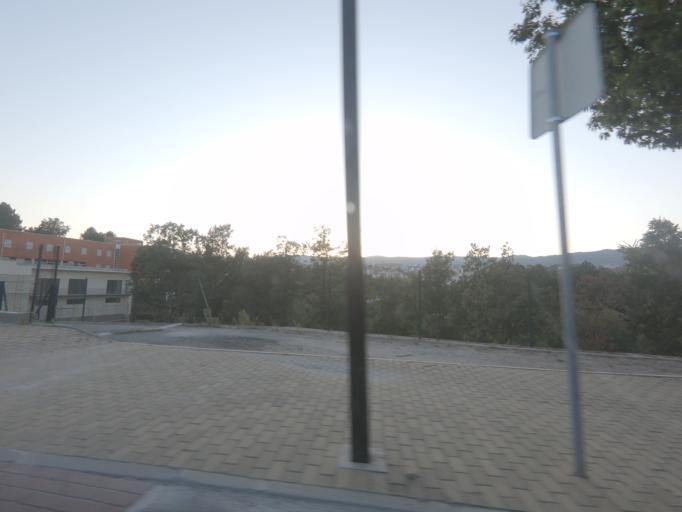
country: PT
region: Vila Real
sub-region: Vila Real
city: Vila Real
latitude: 41.3020
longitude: -7.7311
